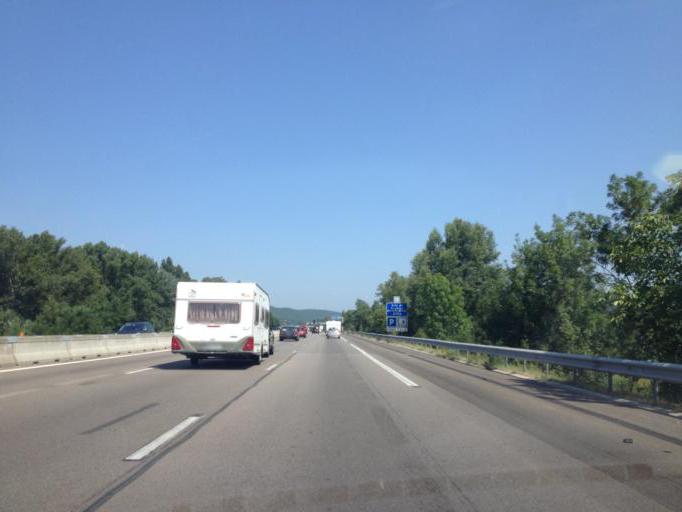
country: FR
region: Rhone-Alpes
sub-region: Departement de la Drome
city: Saint-Marcel-les-Sauzet
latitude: 44.5854
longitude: 4.8030
